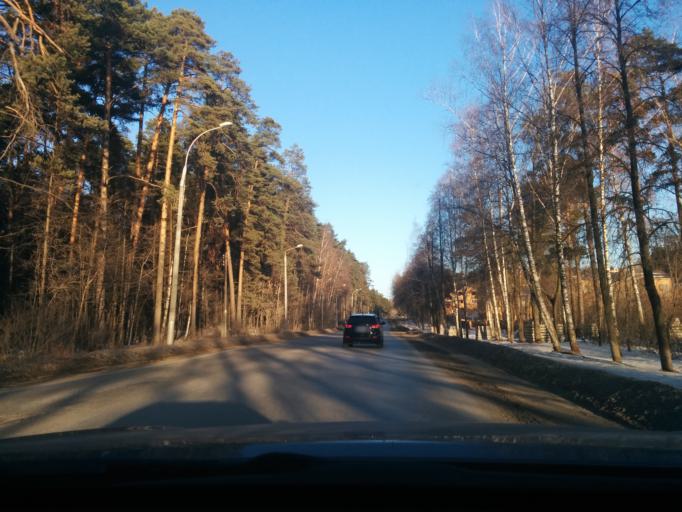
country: RU
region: Perm
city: Kondratovo
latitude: 58.0146
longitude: 55.9918
